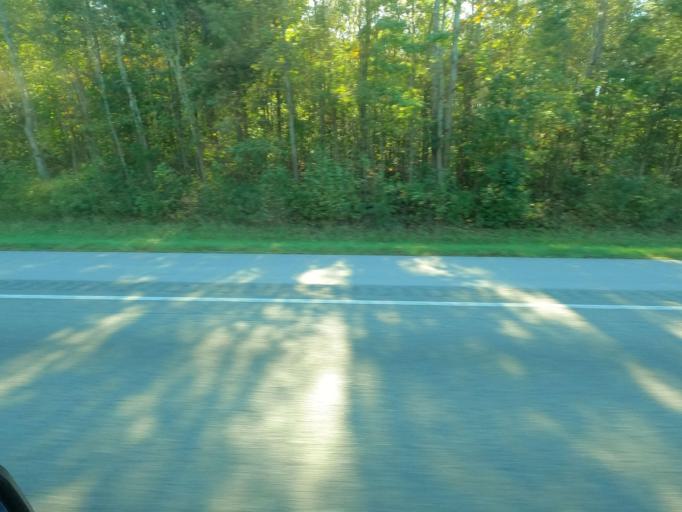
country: US
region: Tennessee
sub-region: Coffee County
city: Manchester
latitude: 35.4072
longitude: -86.0063
